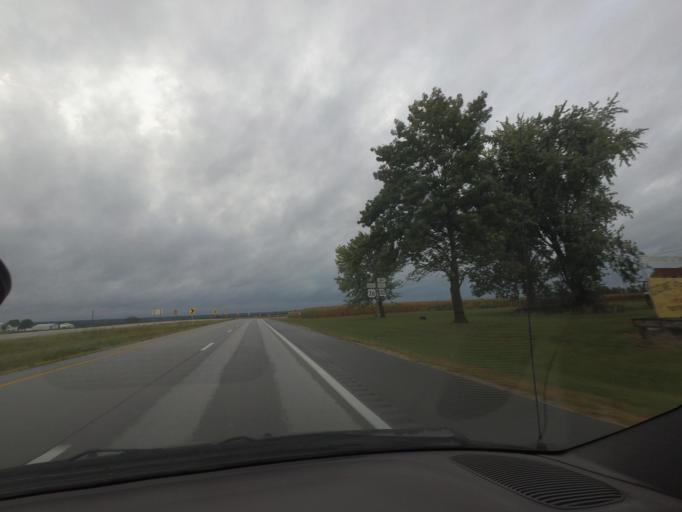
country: US
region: Missouri
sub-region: Shelby County
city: Shelbina
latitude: 39.6744
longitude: -91.9502
